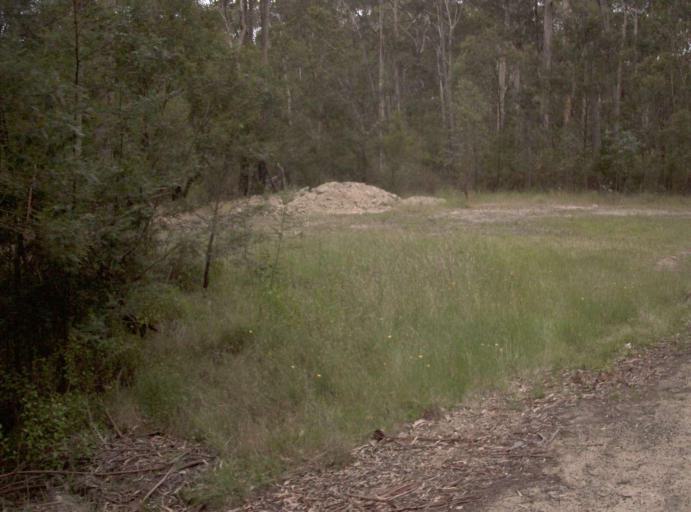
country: AU
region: New South Wales
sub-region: Bombala
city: Bombala
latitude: -37.5008
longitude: 149.1805
